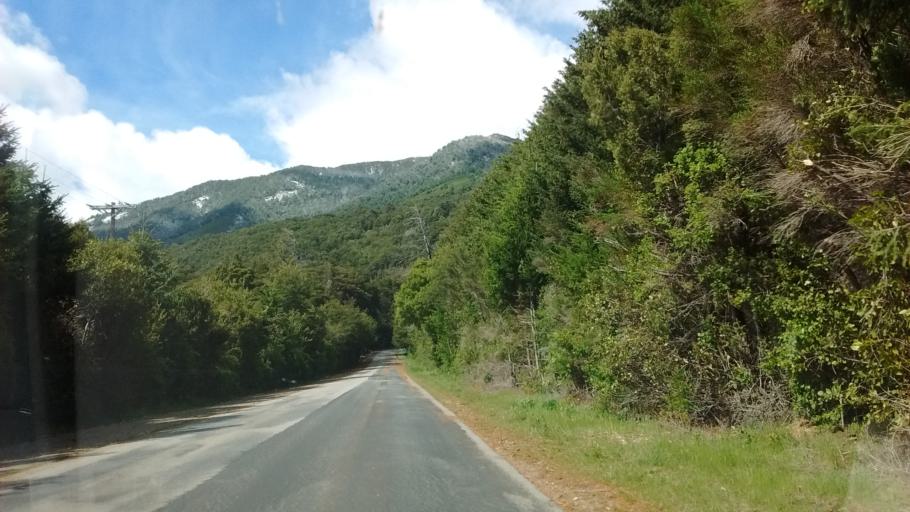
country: AR
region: Rio Negro
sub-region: Departamento de Bariloche
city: San Carlos de Bariloche
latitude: -41.0809
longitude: -71.5450
